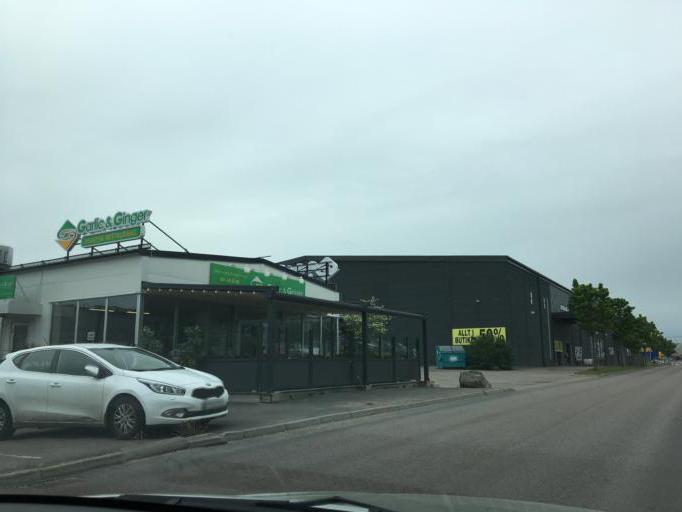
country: SE
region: Vaestmanland
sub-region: Vasteras
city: Vasteras
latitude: 59.6119
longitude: 16.4637
